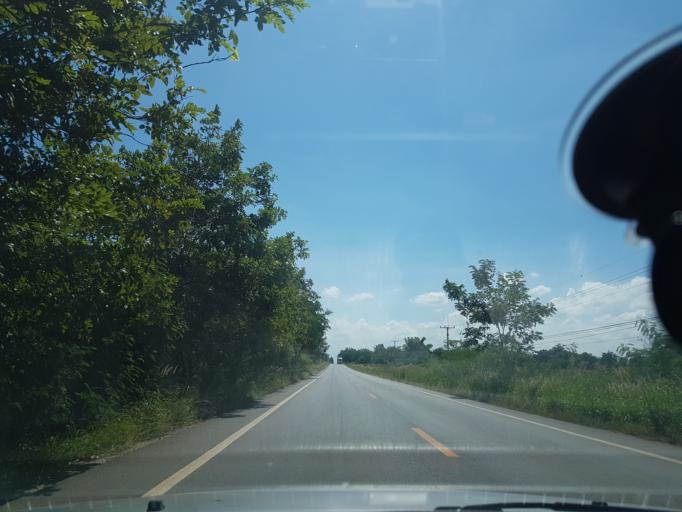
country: TH
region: Lop Buri
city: Phatthana Nikhom
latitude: 14.9720
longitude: 101.0061
